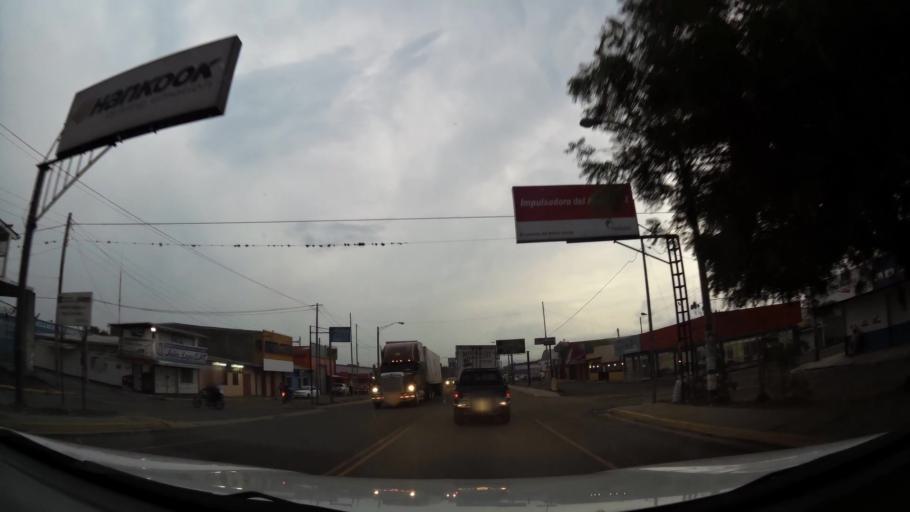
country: NI
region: Esteli
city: Esteli
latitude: 13.0883
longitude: -86.3518
